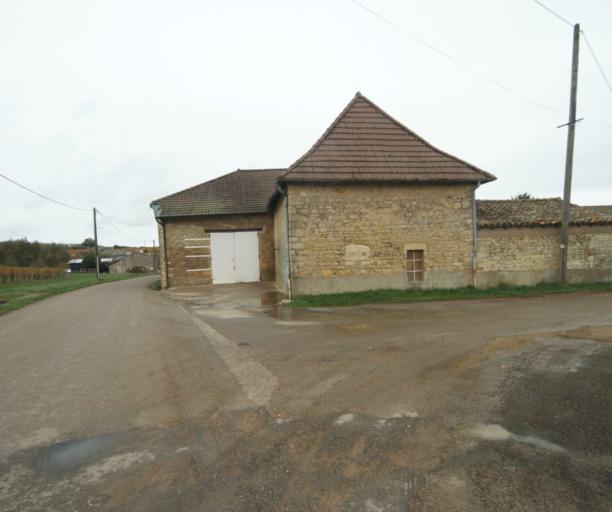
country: FR
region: Rhone-Alpes
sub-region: Departement de l'Ain
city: Pont-de-Vaux
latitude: 46.4741
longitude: 4.8600
